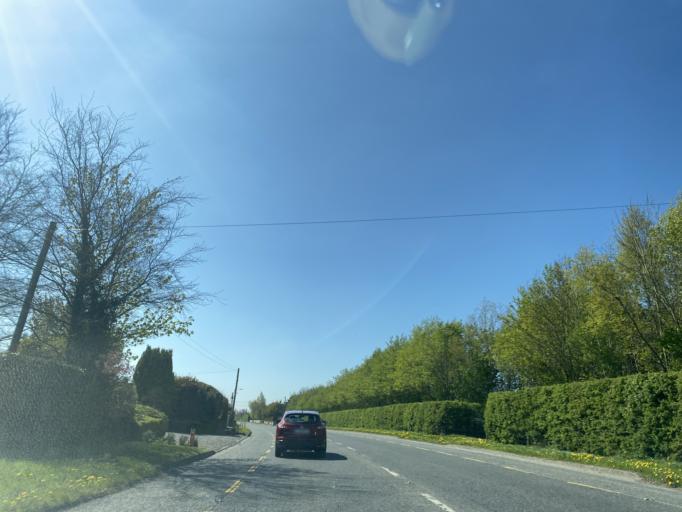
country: IE
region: Leinster
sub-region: Kildare
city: Maynooth
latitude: 53.3326
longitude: -6.6074
